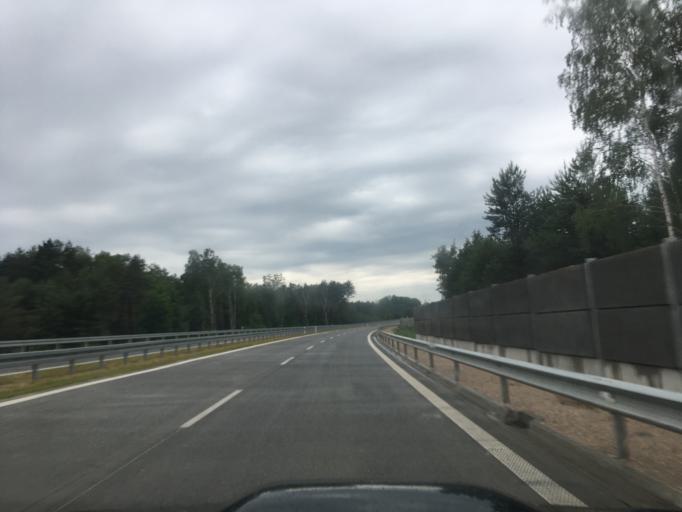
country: PL
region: Masovian Voivodeship
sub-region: Powiat piaseczynski
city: Gora Kalwaria
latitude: 51.9814
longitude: 21.1775
